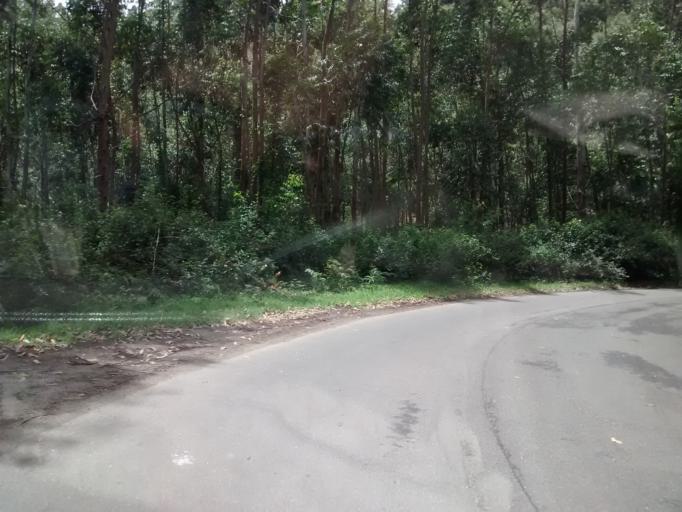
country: IN
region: Kerala
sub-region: Idukki
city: Munnar
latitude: 10.1244
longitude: 77.1591
